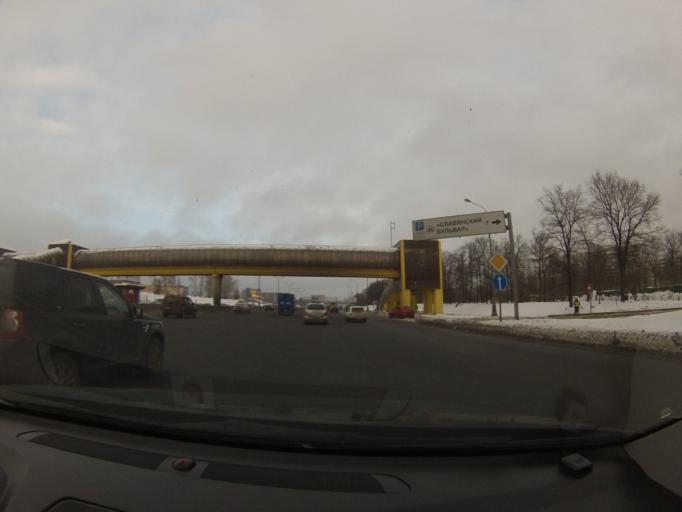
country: RU
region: Moskovskaya
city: Marfino
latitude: 55.7065
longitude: 37.3932
